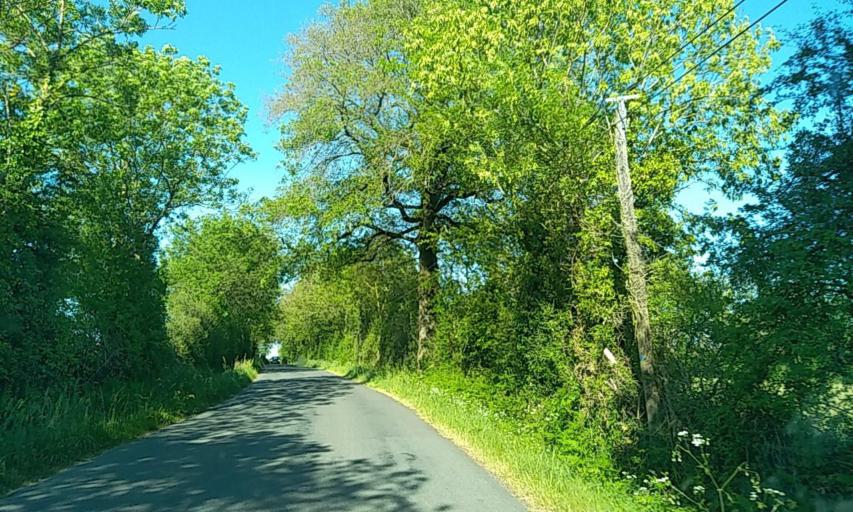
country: FR
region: Poitou-Charentes
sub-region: Departement des Deux-Sevres
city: Boisme
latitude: 46.8031
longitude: -0.4175
